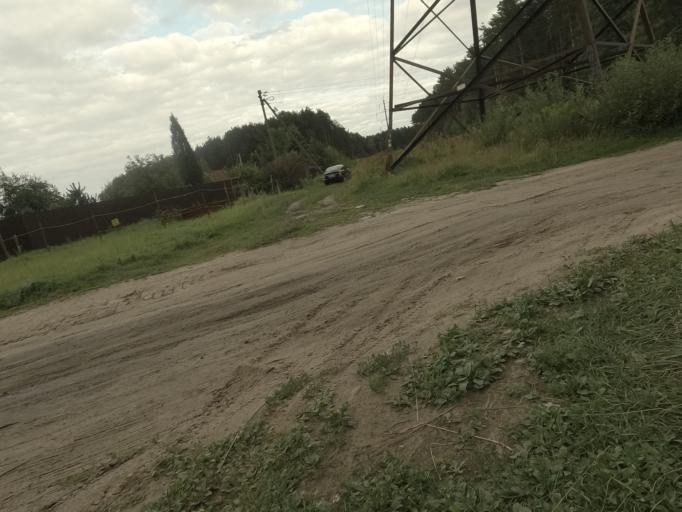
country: RU
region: Leningrad
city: Kirovsk
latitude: 59.8941
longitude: 31.0034
